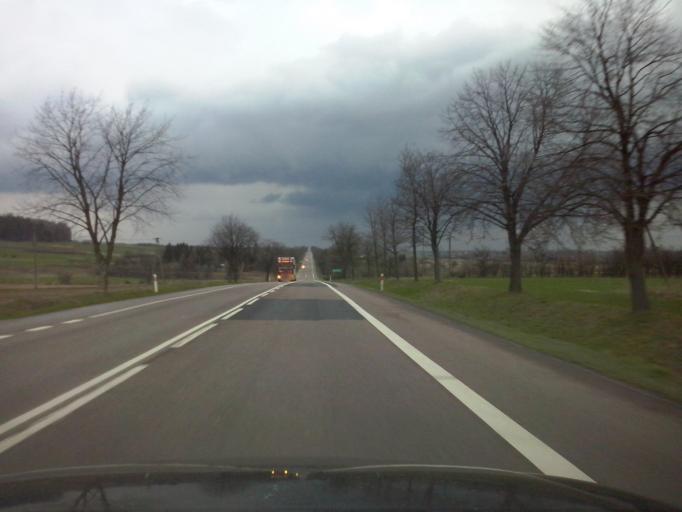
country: PL
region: Lublin Voivodeship
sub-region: Powiat chelmski
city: Rejowiec Fabryczny
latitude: 51.1750
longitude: 23.2566
